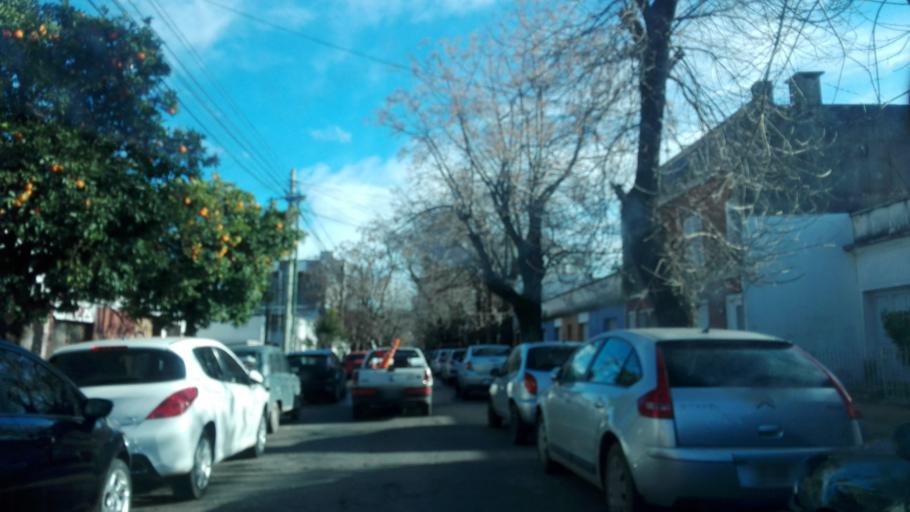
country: AR
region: Buenos Aires
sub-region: Partido de La Plata
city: La Plata
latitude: -34.9234
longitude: -57.9635
